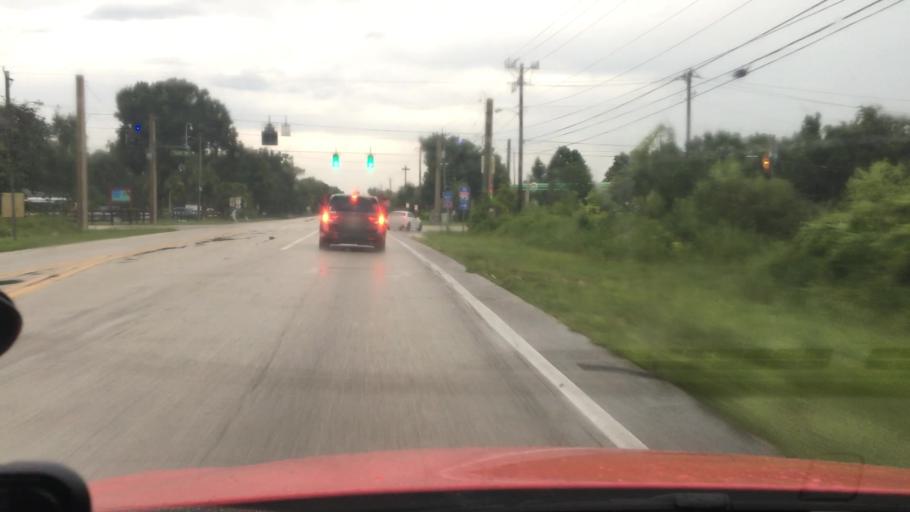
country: US
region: Florida
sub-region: Volusia County
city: Samsula-Spruce Creek
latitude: 29.0823
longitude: -81.0683
